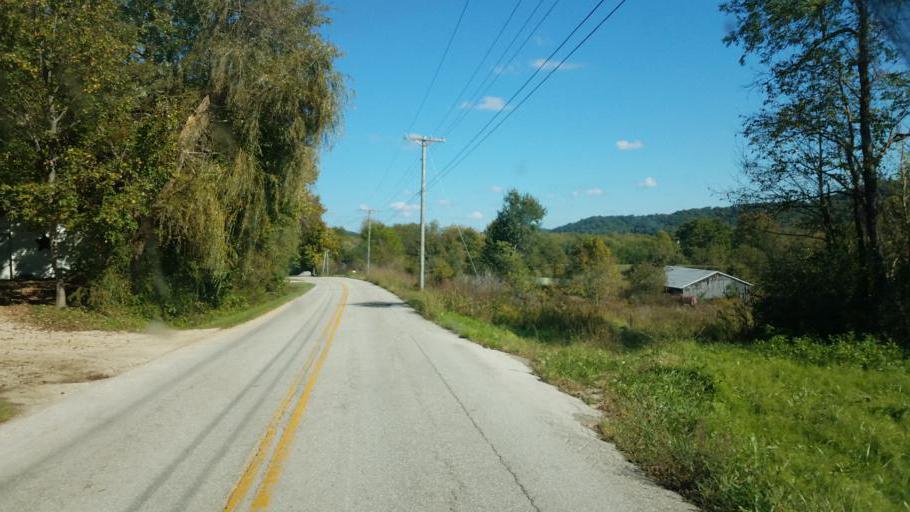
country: US
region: Kentucky
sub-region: Fleming County
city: Flemingsburg
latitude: 38.4668
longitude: -83.5701
